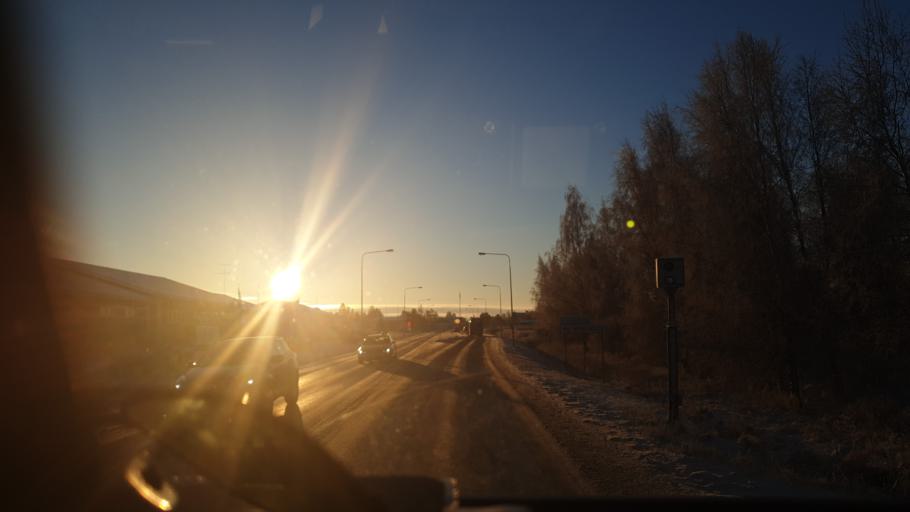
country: FI
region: Northern Ostrobothnia
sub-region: Ylivieska
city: Kalajoki
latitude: 64.2670
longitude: 23.9491
